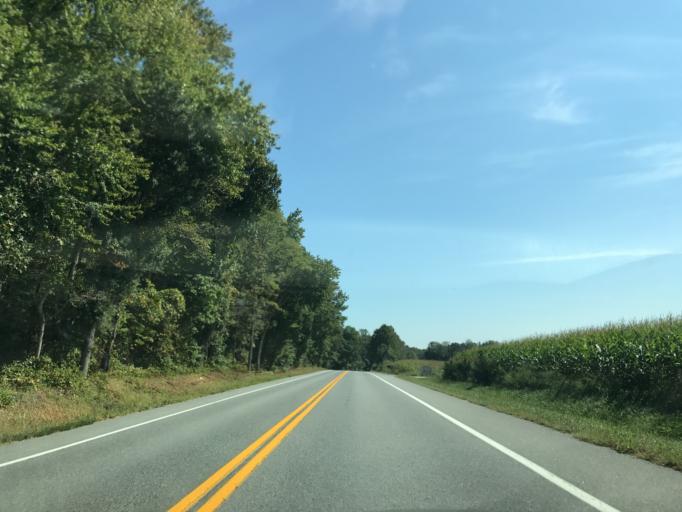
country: US
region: Delaware
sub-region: New Castle County
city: Townsend
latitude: 39.3027
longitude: -75.7863
